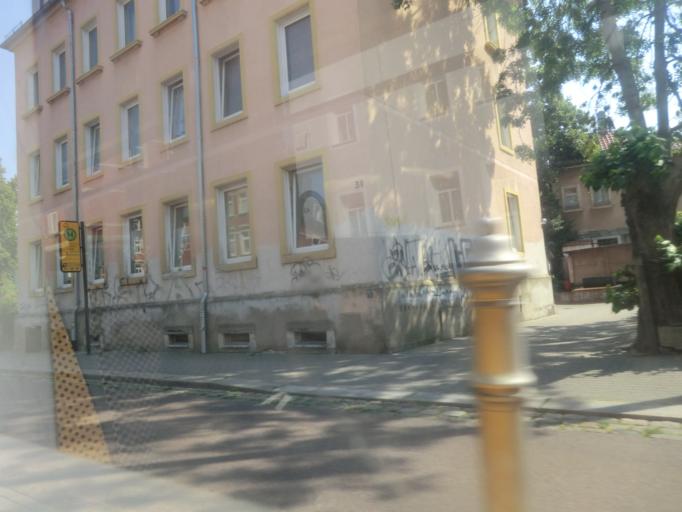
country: DE
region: Saxony
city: Dresden
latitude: 51.0492
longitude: 13.6878
